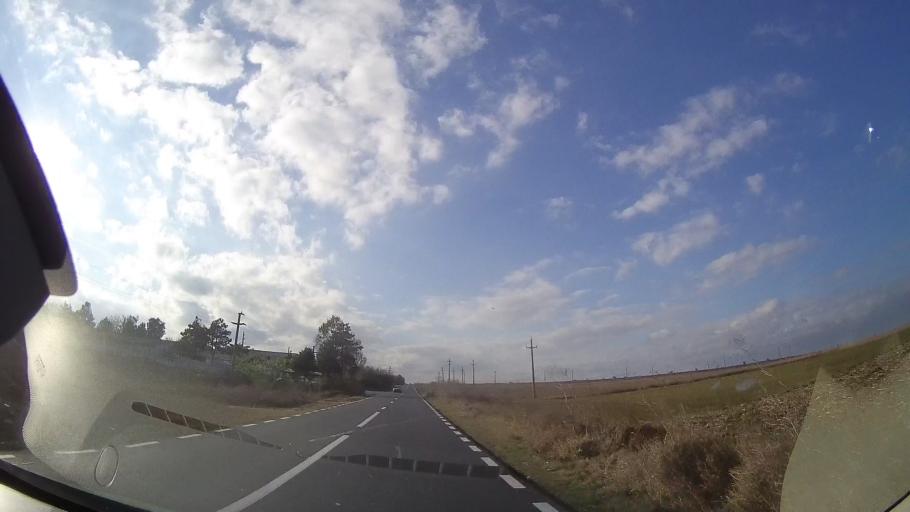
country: RO
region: Constanta
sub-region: Comuna Limanu
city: Limanu
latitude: 43.8236
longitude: 28.5216
